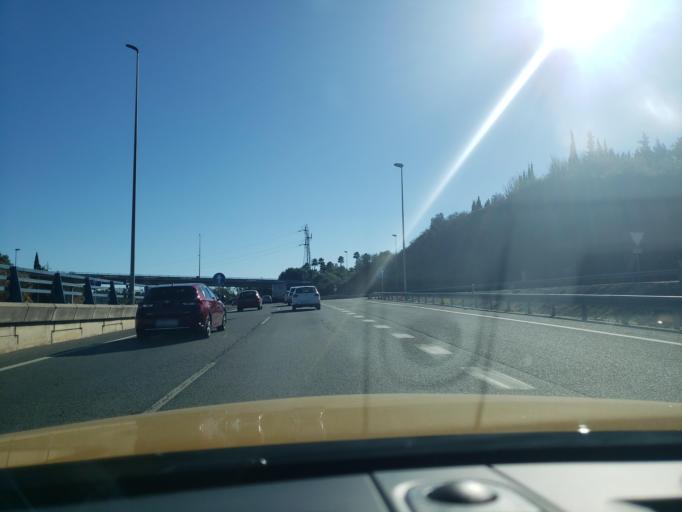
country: ES
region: Andalusia
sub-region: Provincia de Malaga
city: Marbella
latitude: 36.5139
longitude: -4.9328
